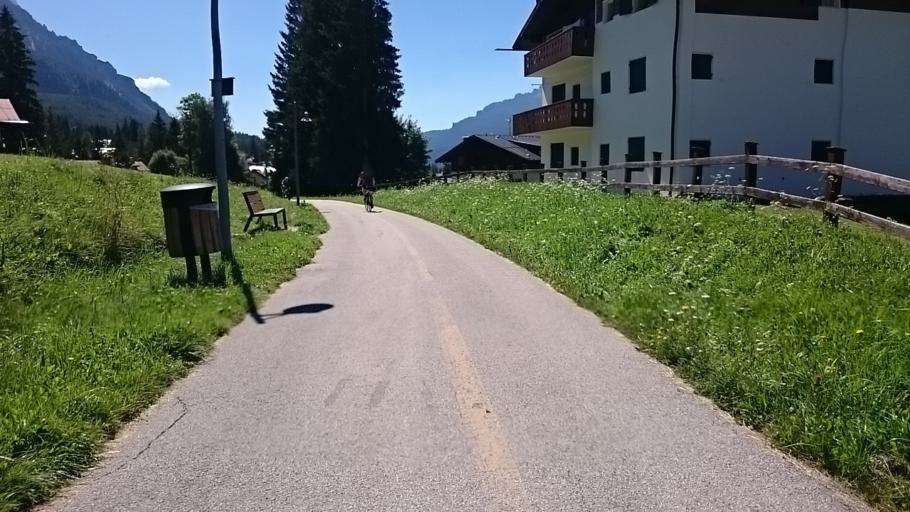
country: IT
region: Veneto
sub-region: Provincia di Belluno
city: Cortina d'Ampezzo
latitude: 46.5471
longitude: 12.1344
